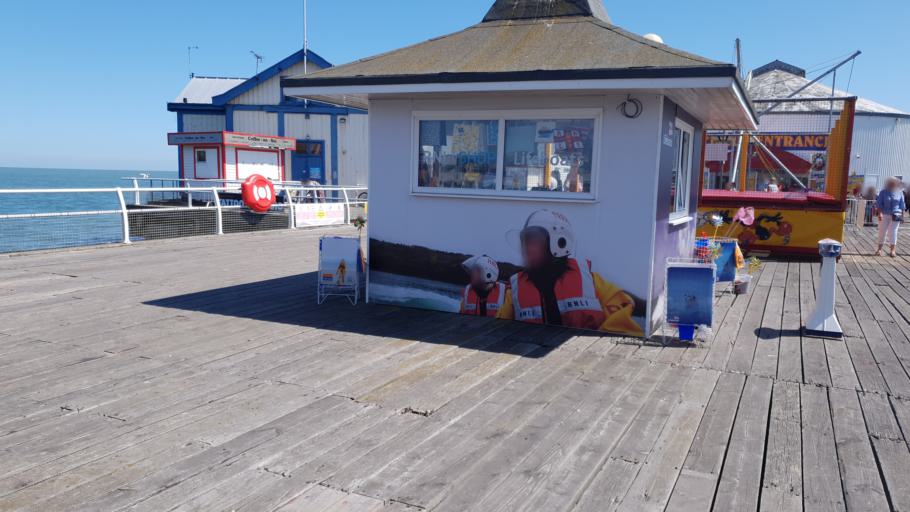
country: GB
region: England
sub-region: Essex
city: Clacton-on-Sea
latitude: 51.7851
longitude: 1.1563
